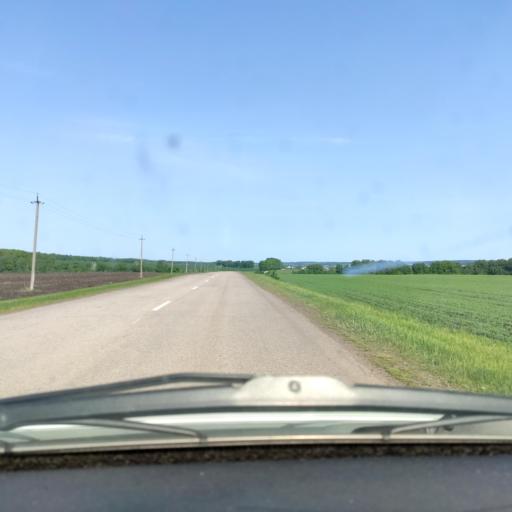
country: RU
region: Bashkortostan
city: Chishmy
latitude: 54.4761
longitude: 55.5490
